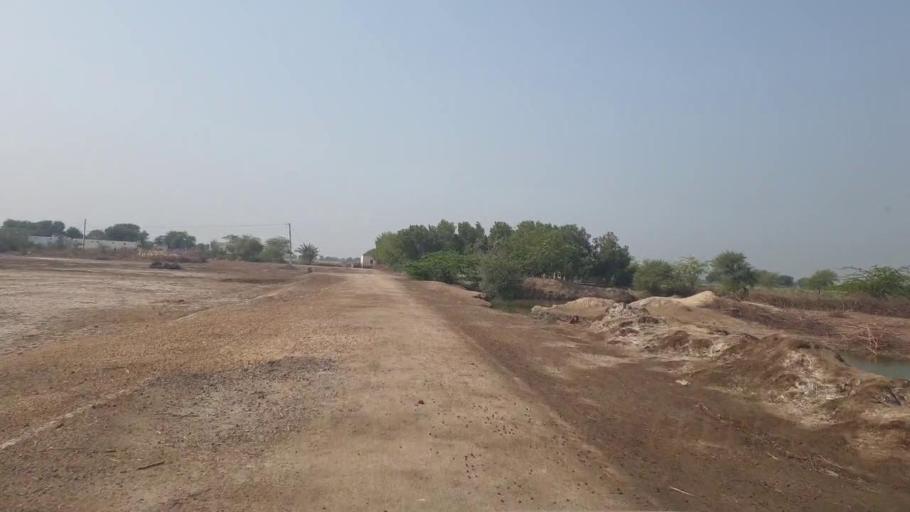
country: PK
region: Sindh
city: Umarkot
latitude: 25.4024
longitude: 69.6919
